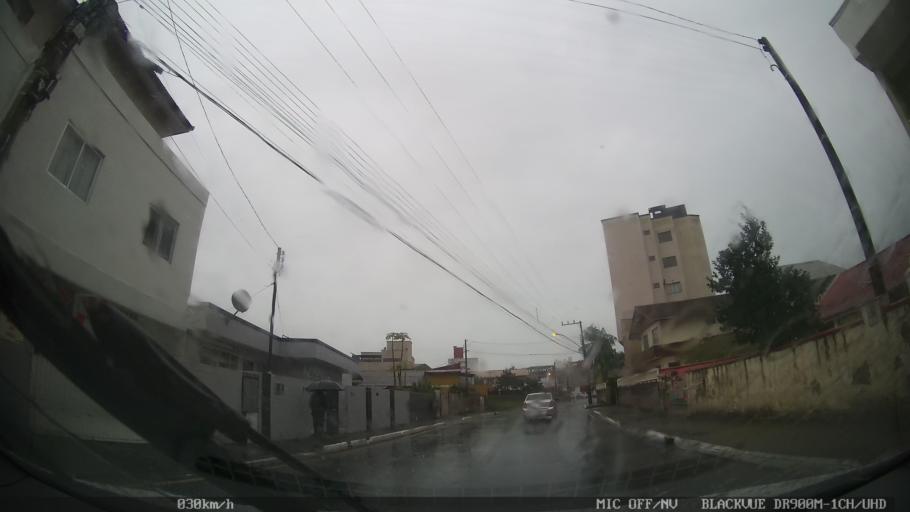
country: BR
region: Santa Catarina
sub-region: Balneario Camboriu
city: Balneario Camboriu
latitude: -27.0105
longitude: -48.6327
